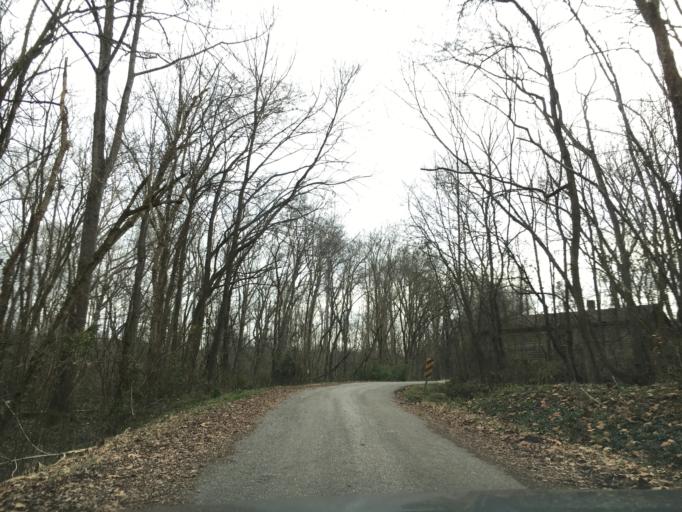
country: US
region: Virginia
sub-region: Powhatan County
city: Powhatan
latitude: 37.4831
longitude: -77.9676
